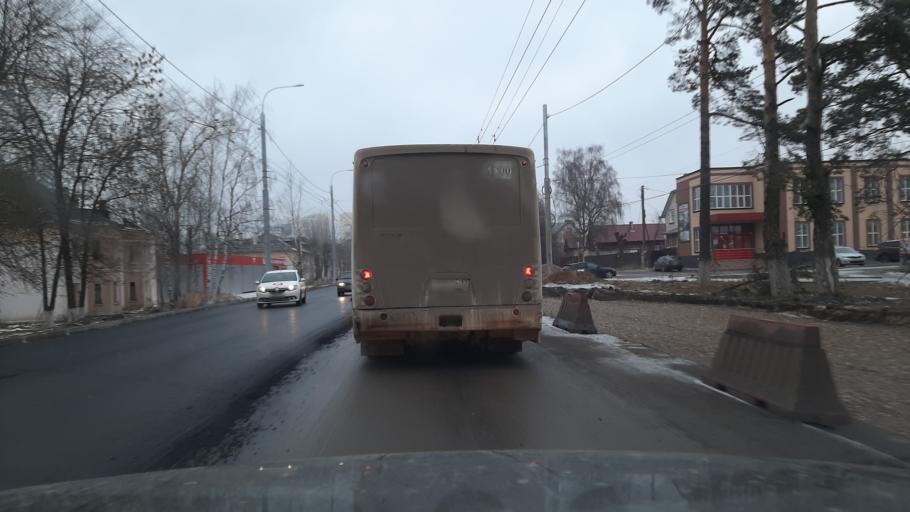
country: RU
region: Ivanovo
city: Kokhma
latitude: 56.9382
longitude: 41.0665
